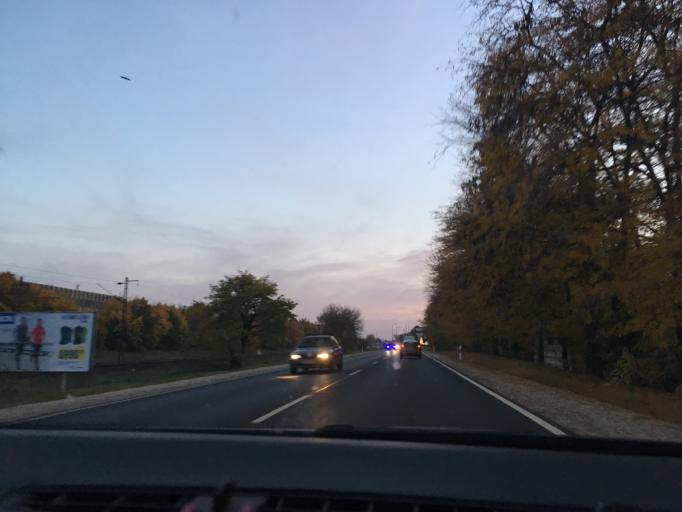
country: HU
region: Hajdu-Bihar
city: Debrecen
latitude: 47.5565
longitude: 21.6504
